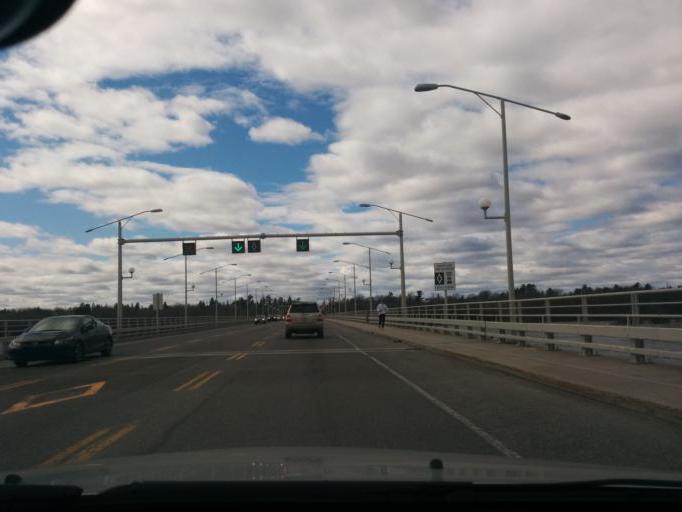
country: CA
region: Ontario
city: Ottawa
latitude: 45.4094
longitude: -75.7589
